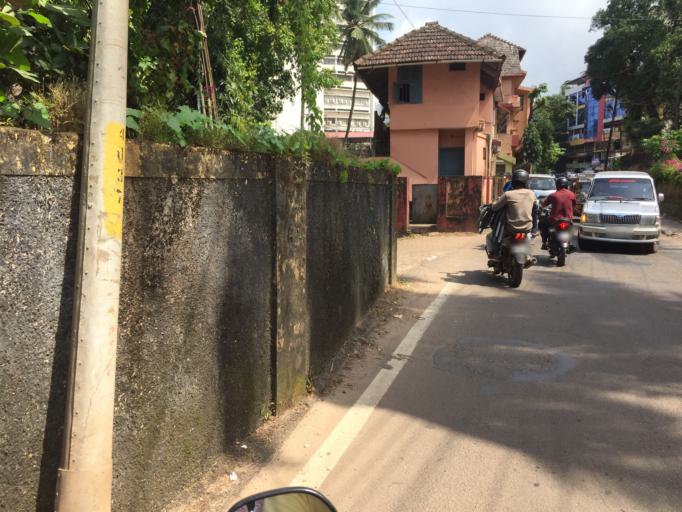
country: IN
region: Karnataka
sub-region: Dakshina Kannada
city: Mangalore
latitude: 12.8708
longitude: 74.8491
